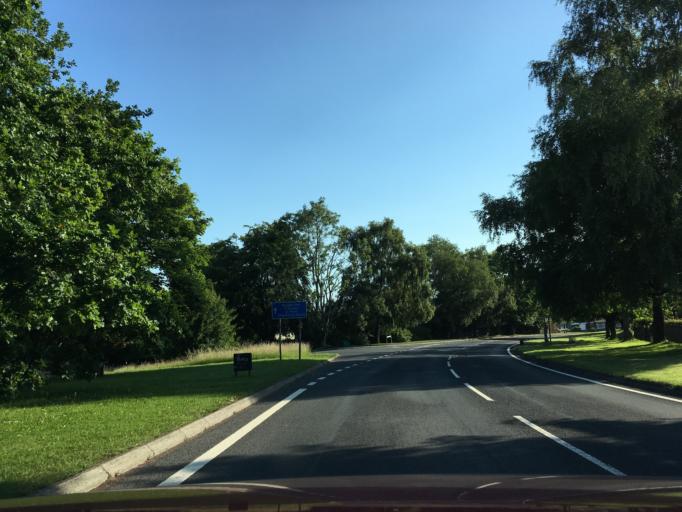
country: GB
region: Wales
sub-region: Monmouthshire
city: Tintern
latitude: 51.7349
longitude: -2.6404
